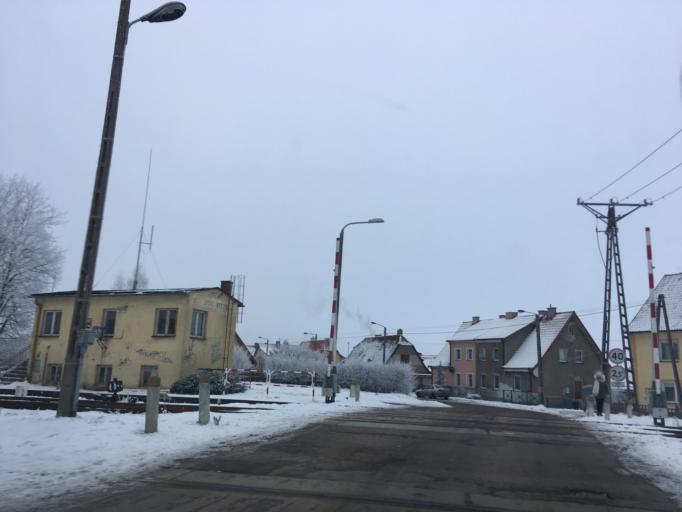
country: PL
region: Warmian-Masurian Voivodeship
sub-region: Powiat olsztynski
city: Biskupiec
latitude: 53.8672
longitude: 20.9598
